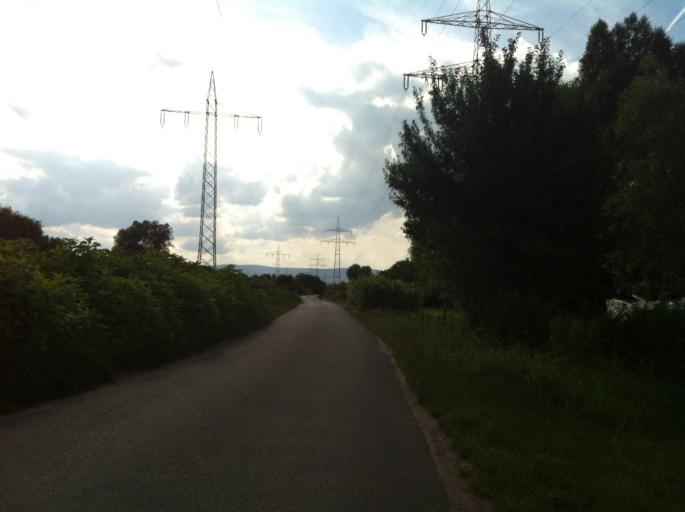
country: DE
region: Rheinland-Pfalz
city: Budenheim
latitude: 50.0272
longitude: 8.2093
